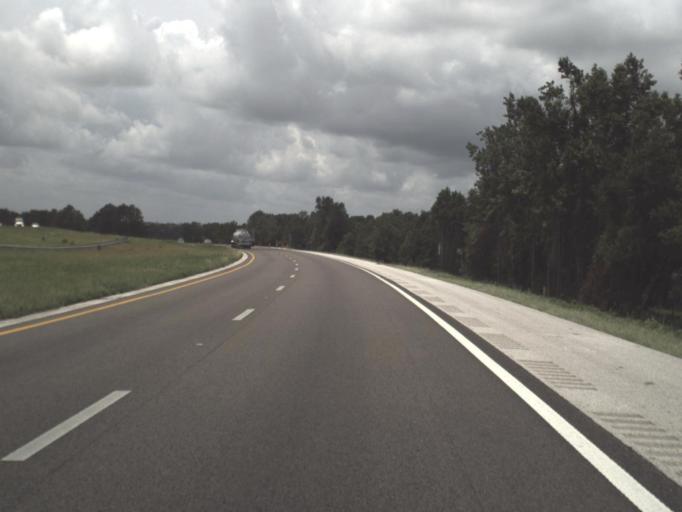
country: US
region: Florida
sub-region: Pasco County
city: San Antonio
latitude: 28.4002
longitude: -82.3151
